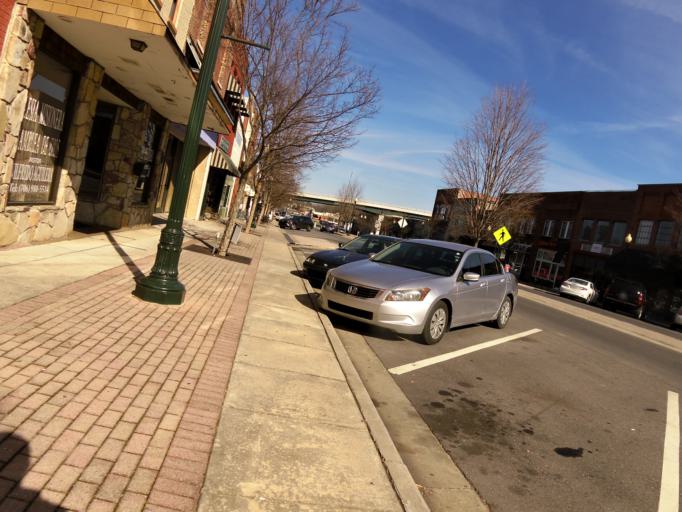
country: US
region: Georgia
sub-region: Whitfield County
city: Dalton
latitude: 34.7730
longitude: -84.9681
